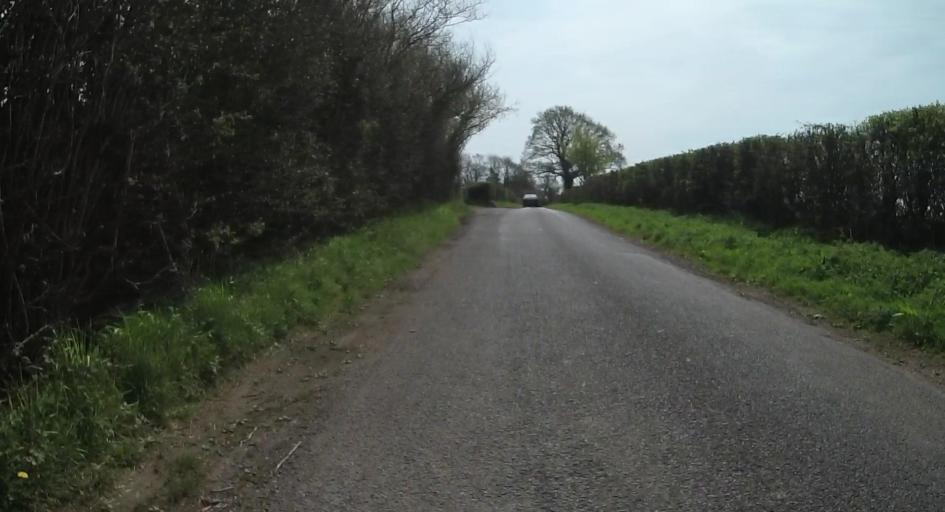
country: GB
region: England
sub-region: Hampshire
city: Alton
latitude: 51.1848
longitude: -0.9693
